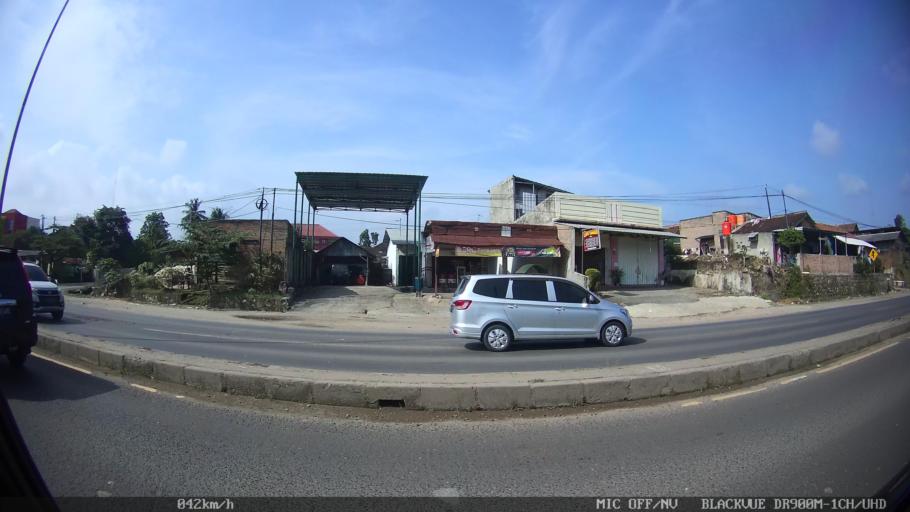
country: ID
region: Lampung
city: Kedaton
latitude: -5.3585
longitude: 105.2533
